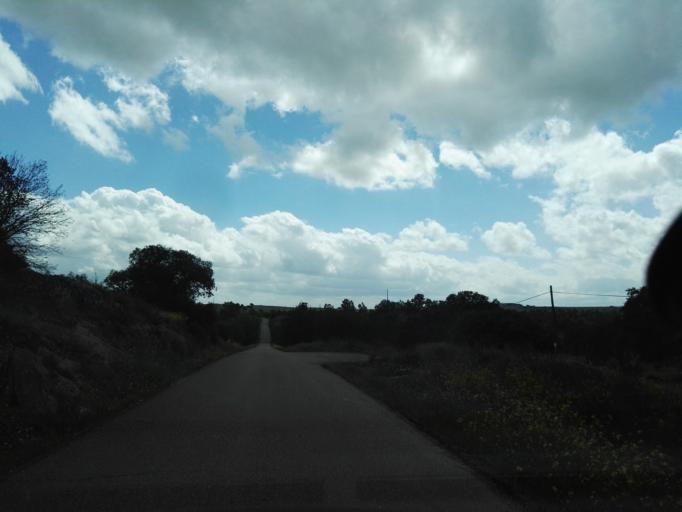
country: PT
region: Portalegre
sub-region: Elvas
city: Elvas
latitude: 38.9768
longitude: -7.1750
